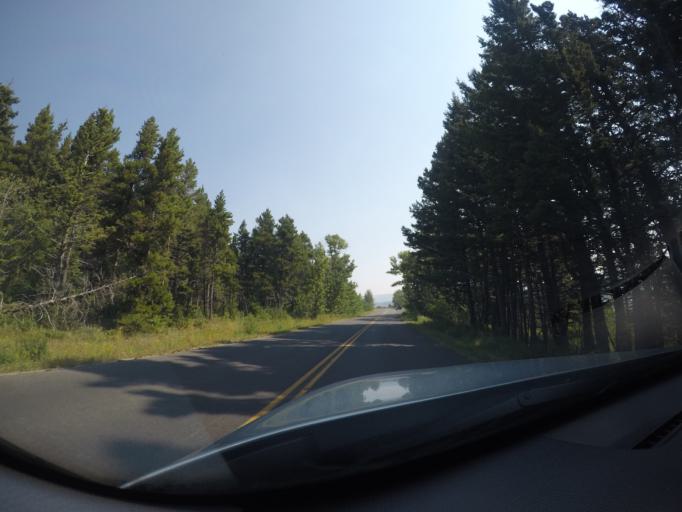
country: US
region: Montana
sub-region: Glacier County
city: North Browning
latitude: 48.7096
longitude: -113.4896
